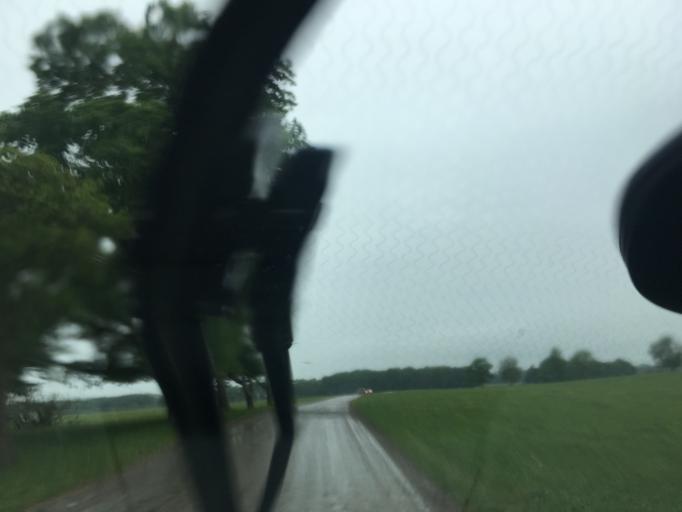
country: SE
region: Skane
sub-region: Lunds Kommun
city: Veberod
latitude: 55.6640
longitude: 13.4841
